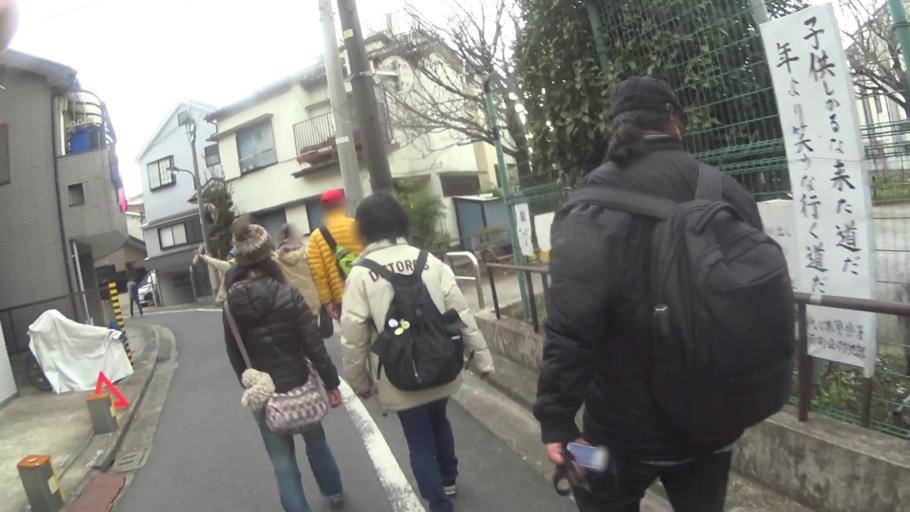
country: JP
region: Tokyo
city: Tokyo
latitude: 35.6835
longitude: 139.6787
